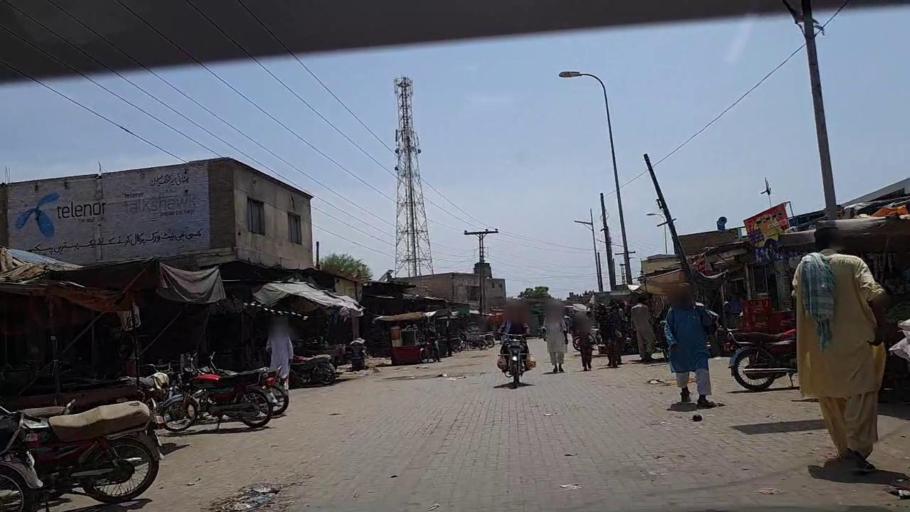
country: PK
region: Sindh
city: Khanpur
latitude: 27.8451
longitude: 69.4158
